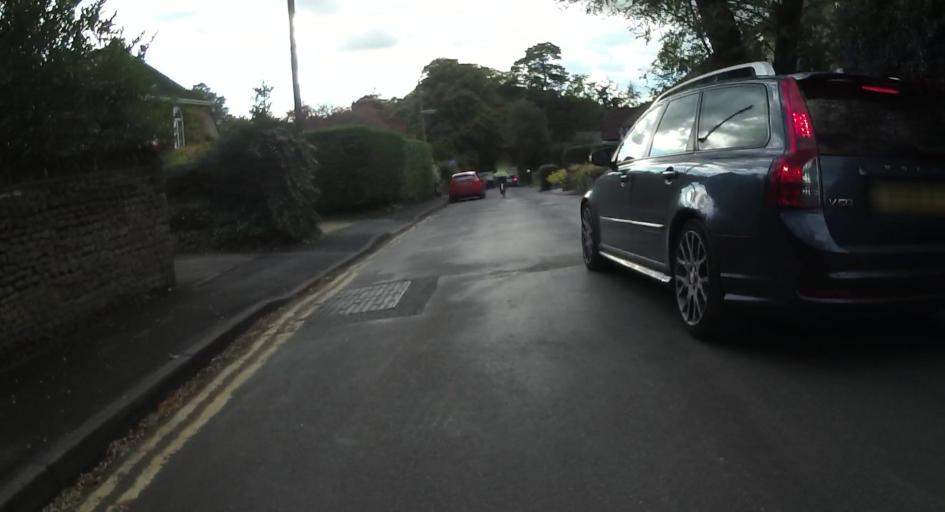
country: GB
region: England
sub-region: Surrey
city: Farnham
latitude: 51.1963
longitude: -0.7928
